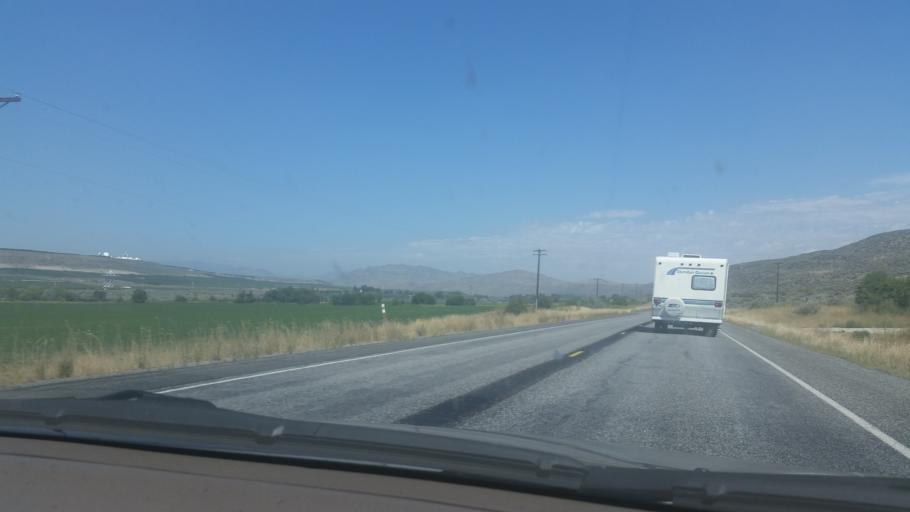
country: US
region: Washington
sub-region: Okanogan County
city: Brewster
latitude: 48.1200
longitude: -119.6763
